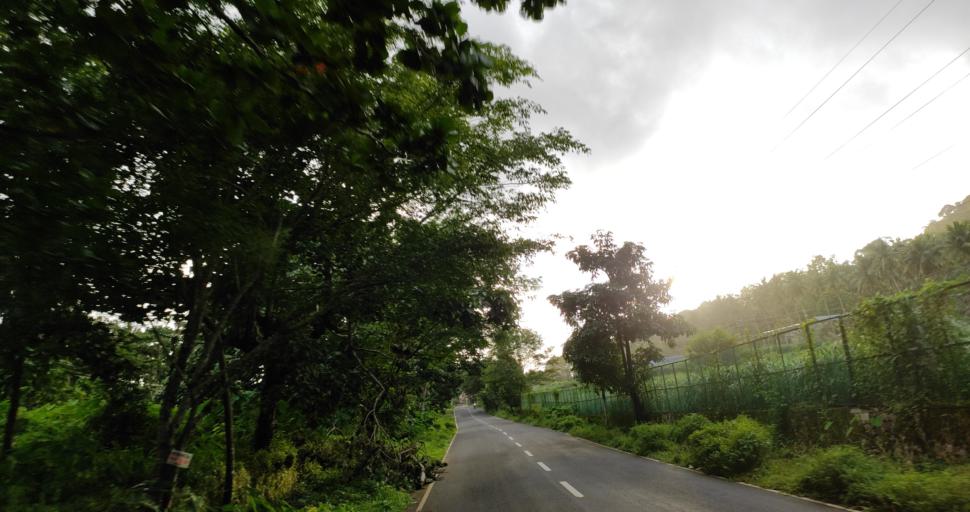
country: IN
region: Kerala
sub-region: Thrissur District
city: Kizhake Chalakudi
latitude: 10.2991
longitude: 76.4356
